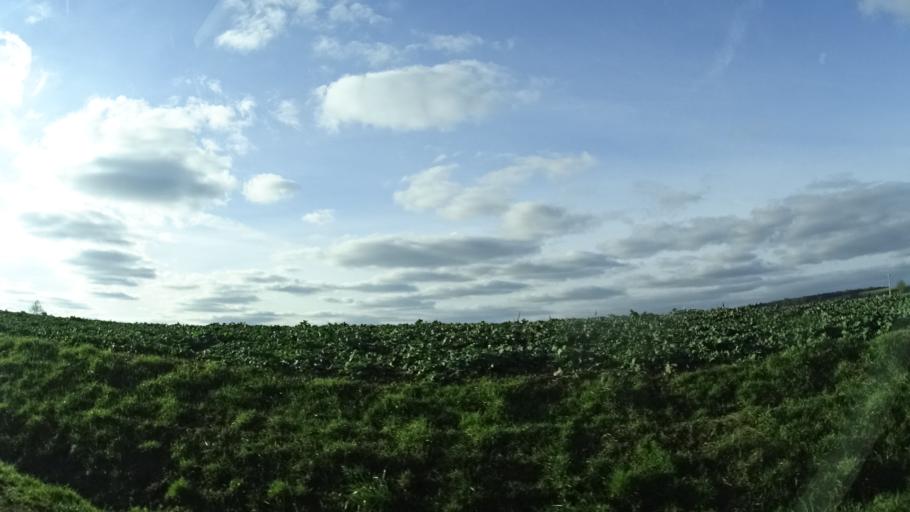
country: DE
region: Bavaria
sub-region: Regierungsbezirk Unterfranken
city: Rollbach
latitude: 49.7666
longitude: 9.2469
